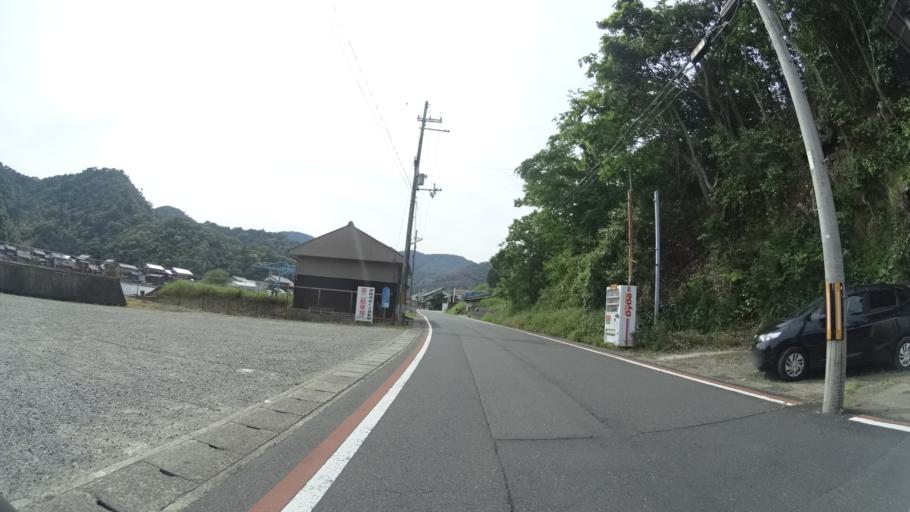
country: JP
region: Kyoto
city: Miyazu
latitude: 35.6714
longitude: 135.2767
